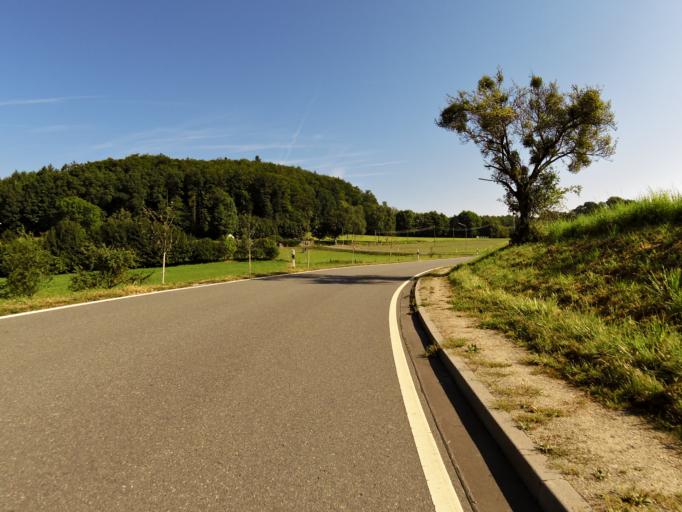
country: DE
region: Hesse
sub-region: Regierungsbezirk Darmstadt
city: Lindenfels
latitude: 49.6915
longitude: 8.7226
